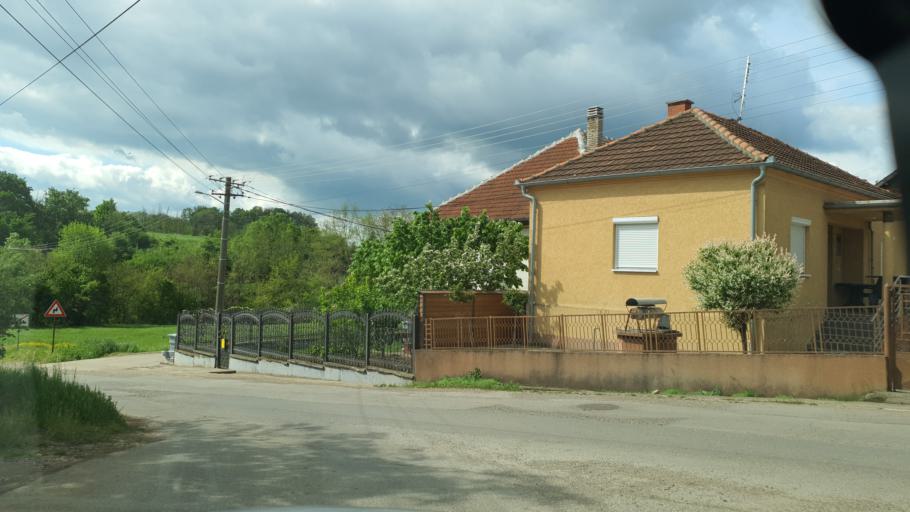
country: RS
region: Central Serbia
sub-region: Pomoravski Okrug
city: Paracin
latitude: 43.9370
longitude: 21.4929
